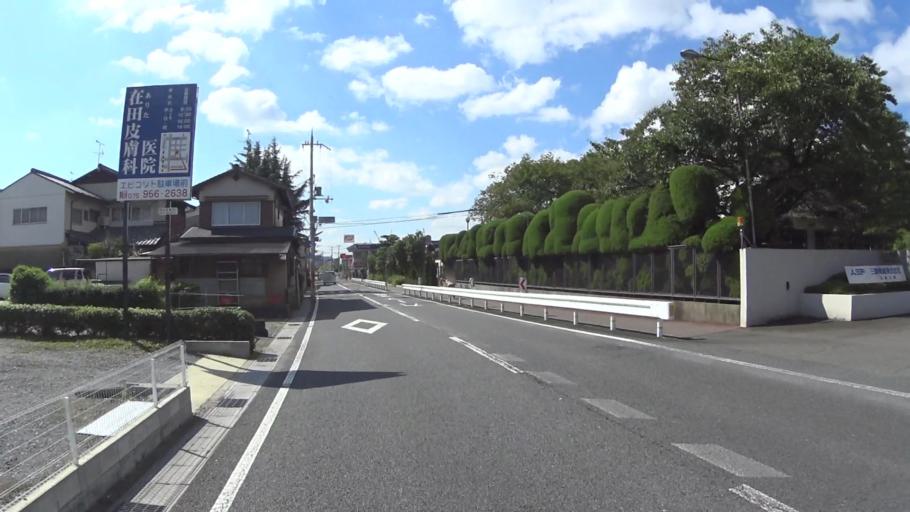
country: JP
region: Kyoto
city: Muko
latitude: 34.9285
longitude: 135.7000
